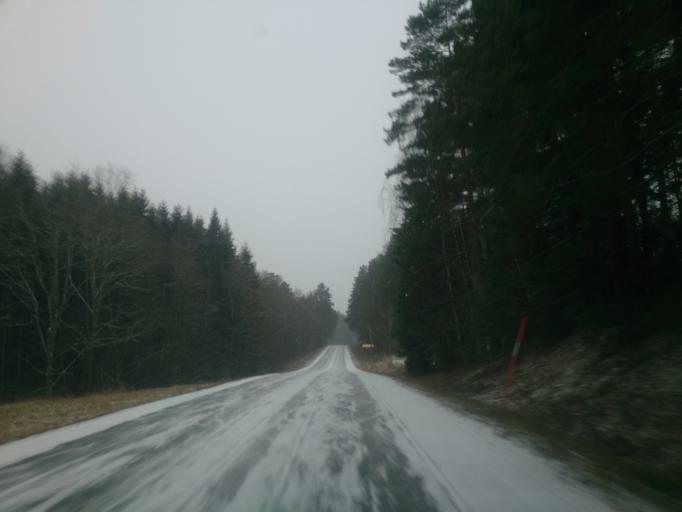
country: SE
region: OEstergoetland
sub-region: Norrkopings Kommun
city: Norrkoping
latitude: 58.4907
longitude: 16.1141
